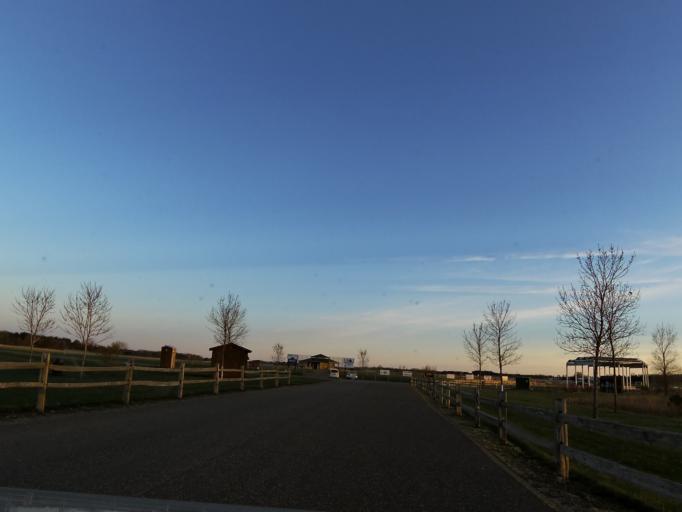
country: US
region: Minnesota
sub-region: Washington County
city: Lakeland
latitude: 44.9550
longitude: -92.7879
